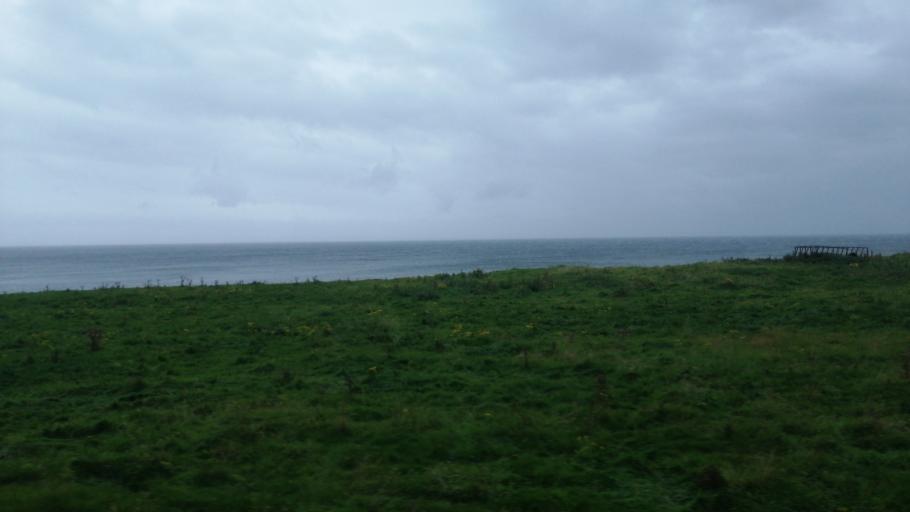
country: GB
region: Scotland
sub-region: Highland
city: Brora
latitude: 58.0568
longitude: -3.8063
